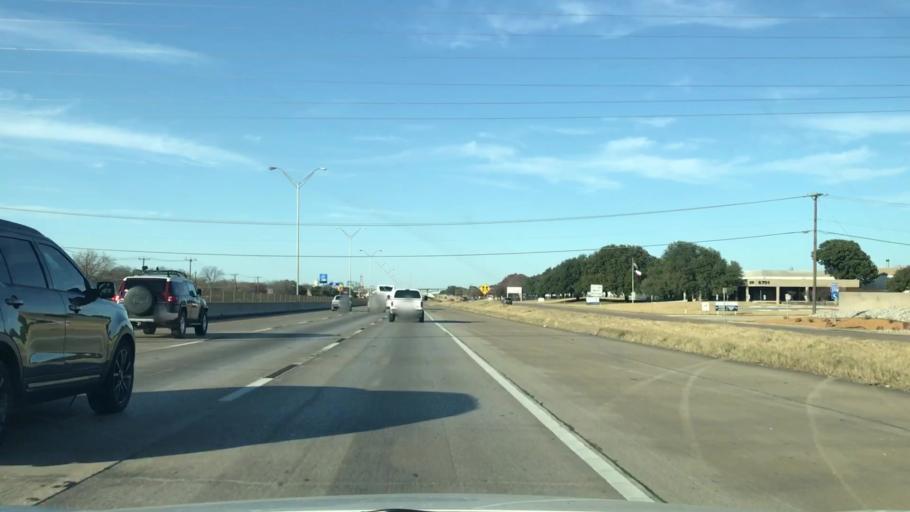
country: US
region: Texas
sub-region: Tarrant County
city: Edgecliff Village
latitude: 32.6449
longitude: -97.3214
